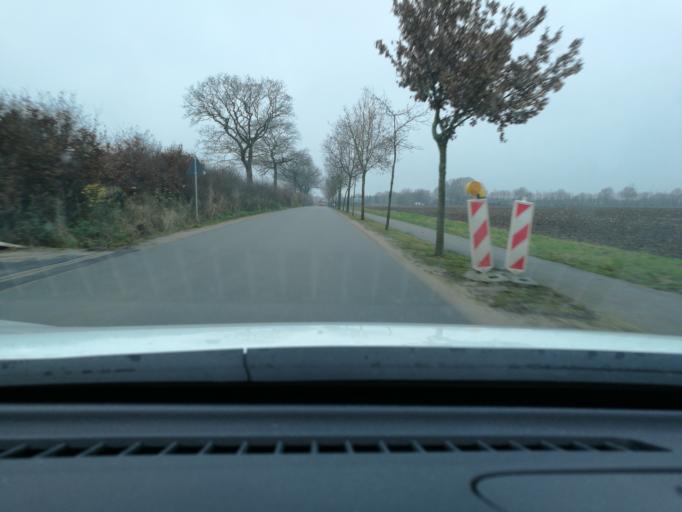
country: DE
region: Schleswig-Holstein
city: Borgstedt
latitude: 54.3352
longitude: 9.7010
